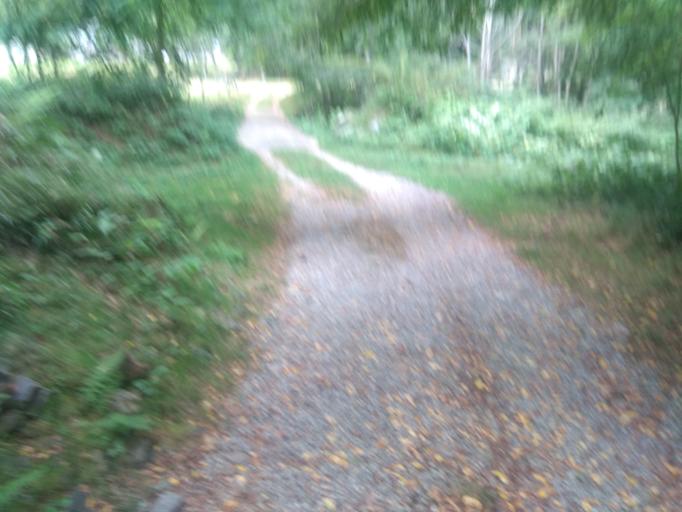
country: IT
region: Piedmont
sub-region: Provincia di Vercelli
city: Vocca
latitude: 45.8249
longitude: 8.1710
